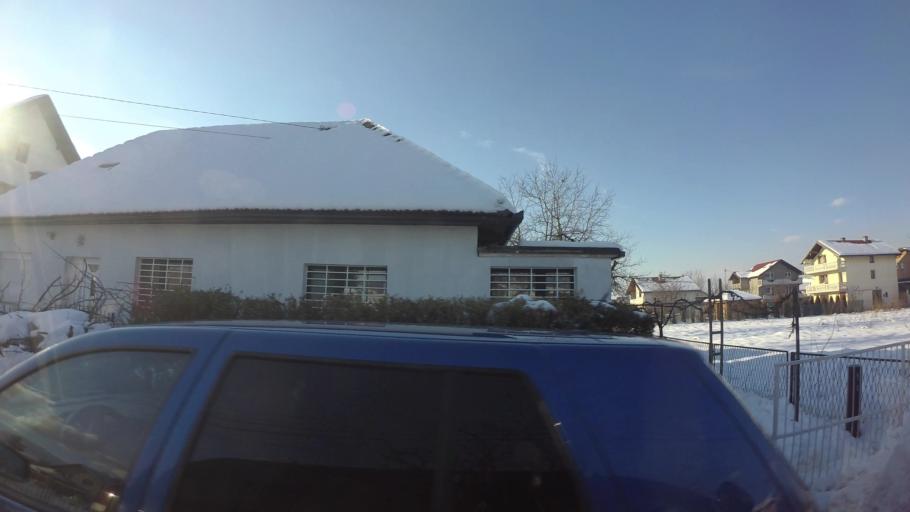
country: BA
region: Federation of Bosnia and Herzegovina
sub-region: Kanton Sarajevo
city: Sarajevo
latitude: 43.8177
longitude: 18.3388
